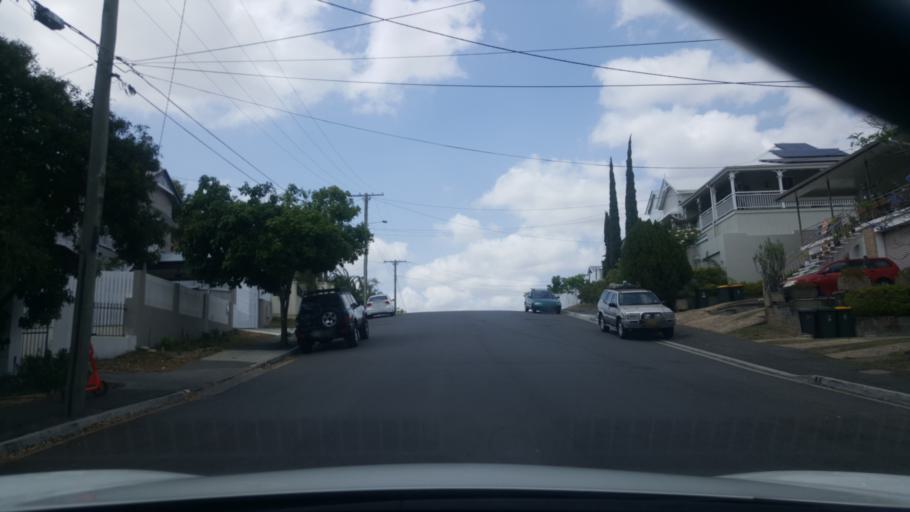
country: AU
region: Queensland
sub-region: Brisbane
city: South Brisbane
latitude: -27.4867
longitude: 153.0226
